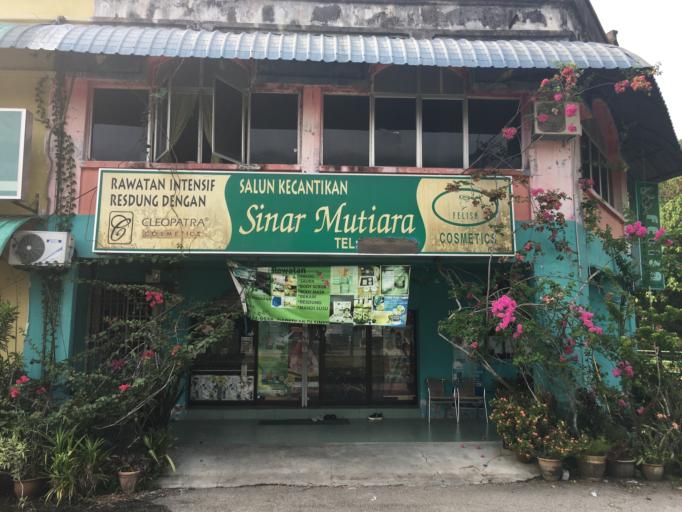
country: MY
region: Kedah
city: Kulim
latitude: 5.3882
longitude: 100.5632
